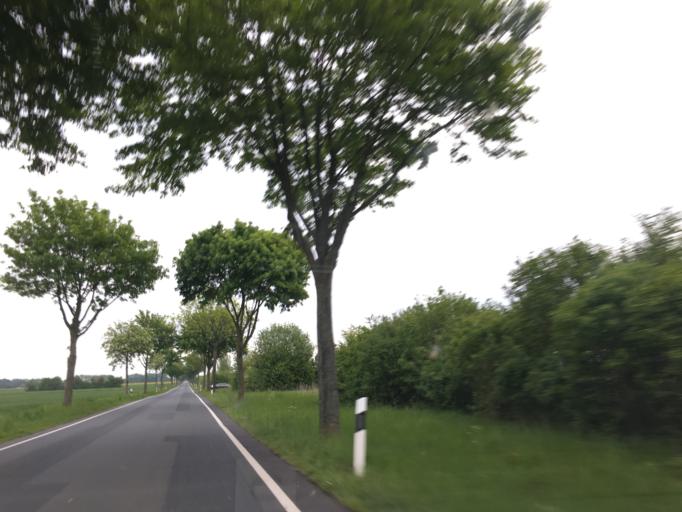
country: DE
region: Lower Saxony
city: Haste
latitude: 52.3800
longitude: 9.4271
